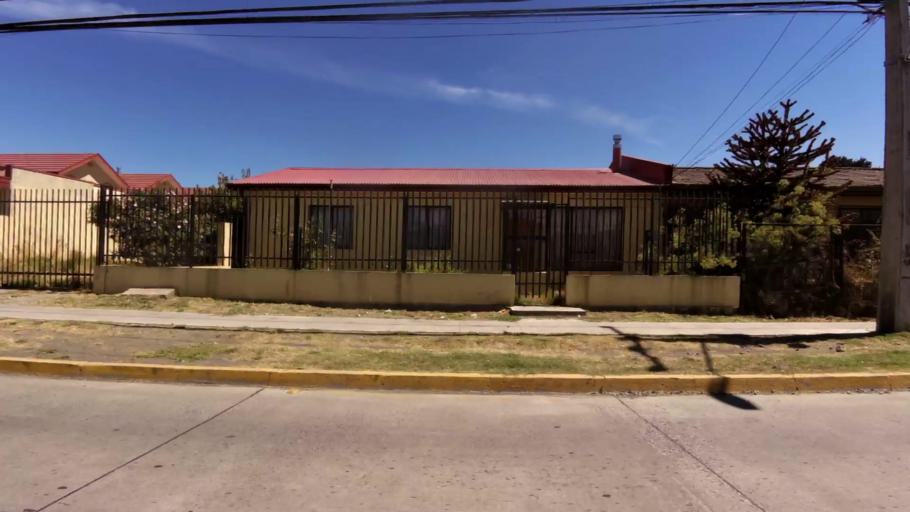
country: CL
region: Biobio
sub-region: Provincia de Concepcion
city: Talcahuano
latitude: -36.7589
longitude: -73.0864
